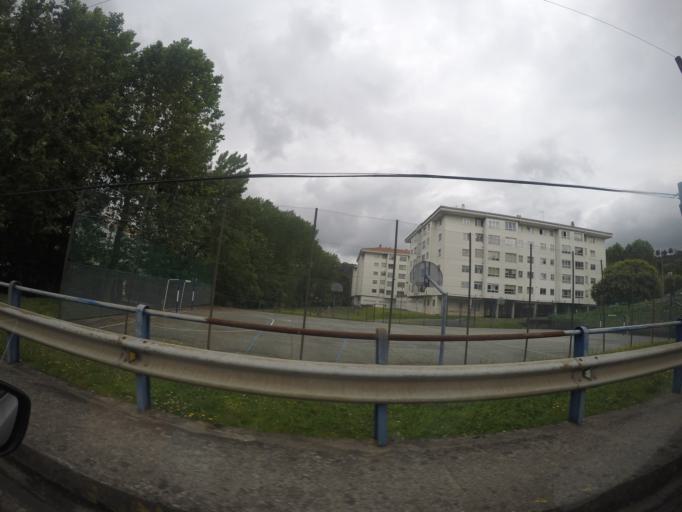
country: ES
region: Galicia
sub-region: Provincia da Coruna
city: Culleredo
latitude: 43.3071
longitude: -8.3829
